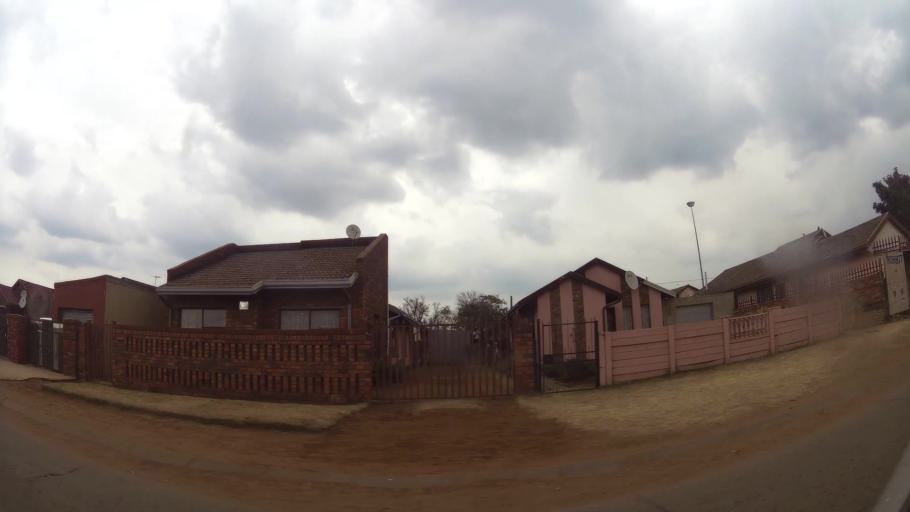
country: ZA
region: Gauteng
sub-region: Ekurhuleni Metropolitan Municipality
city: Germiston
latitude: -26.3600
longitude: 28.1499
